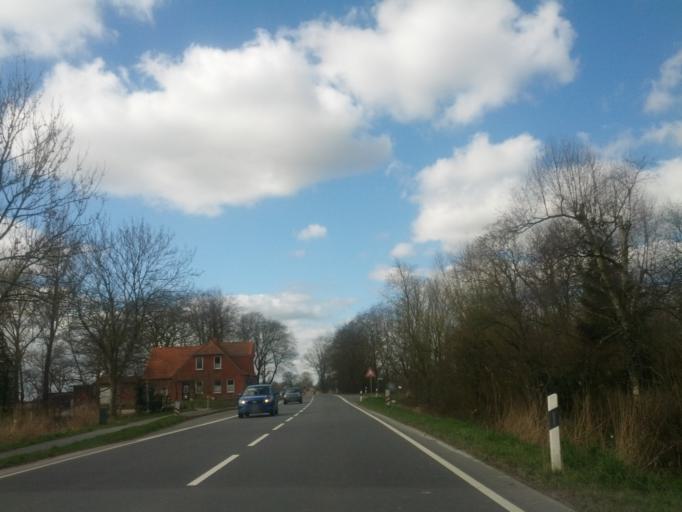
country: DE
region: Lower Saxony
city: Jever
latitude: 53.5792
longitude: 7.8532
